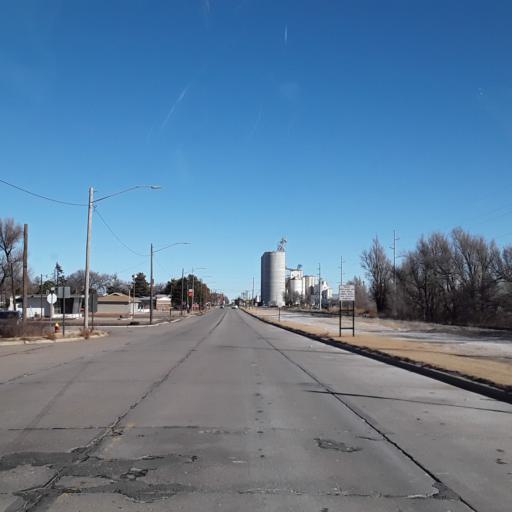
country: US
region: Kansas
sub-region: Pawnee County
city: Larned
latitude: 38.1721
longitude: -99.1046
